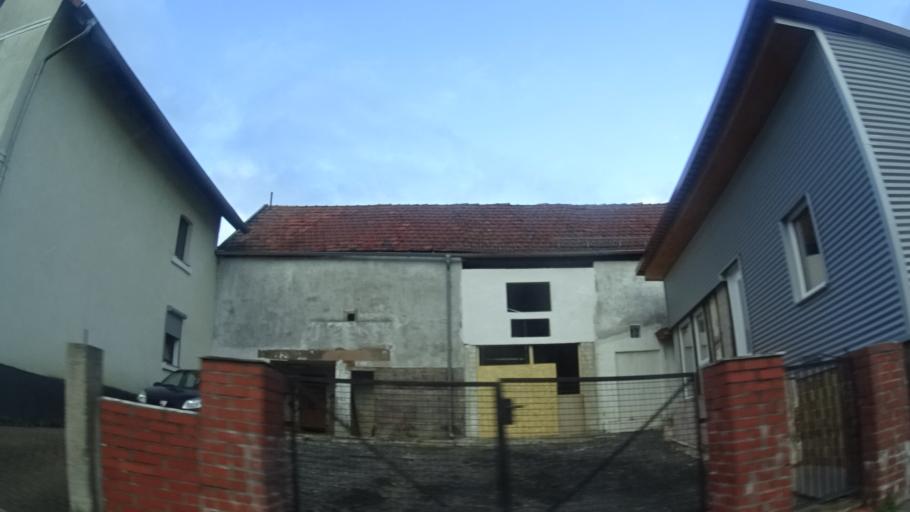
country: DE
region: Hesse
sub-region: Regierungsbezirk Kassel
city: Flieden
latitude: 50.4512
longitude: 9.5748
